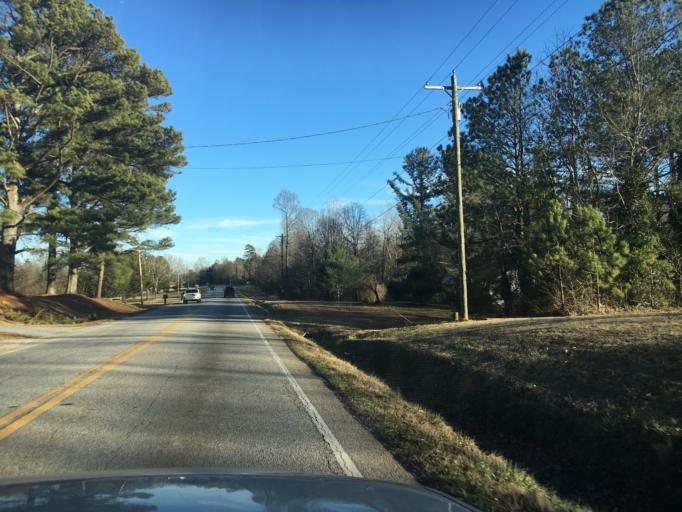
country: US
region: Georgia
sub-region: Habersham County
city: Demorest
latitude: 34.5509
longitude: -83.5656
